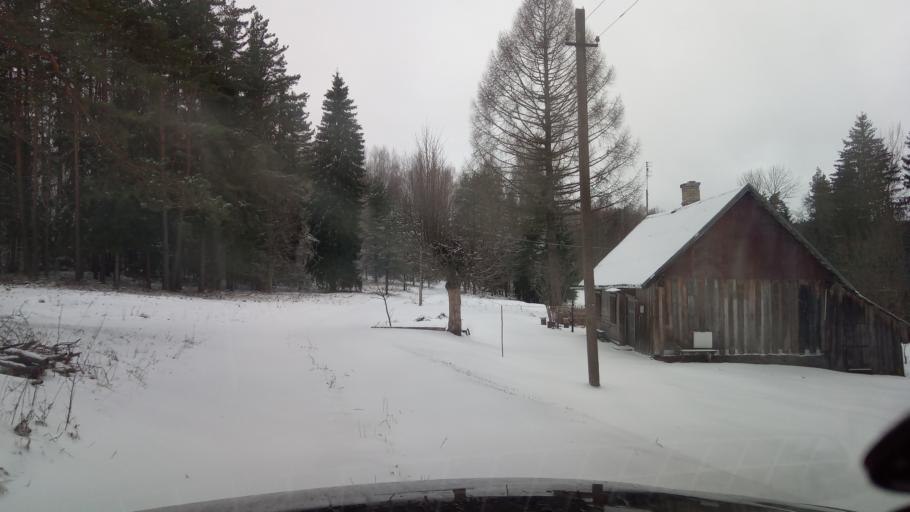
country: LT
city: Zarasai
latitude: 55.6620
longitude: 26.0963
